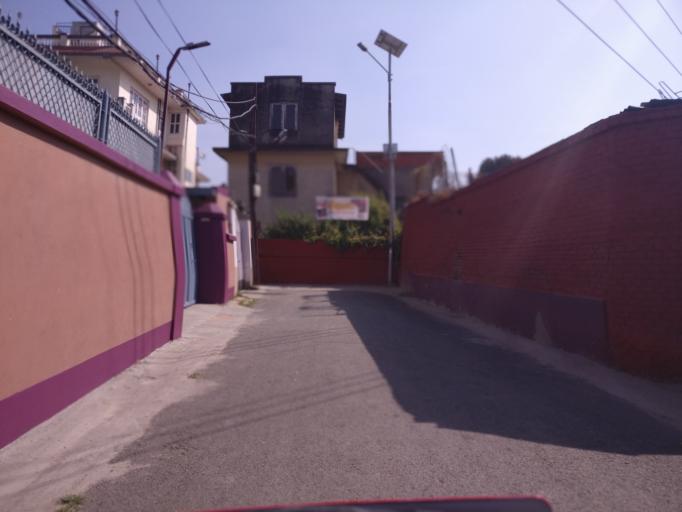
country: NP
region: Central Region
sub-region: Bagmati Zone
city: Patan
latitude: 27.6702
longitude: 85.3179
